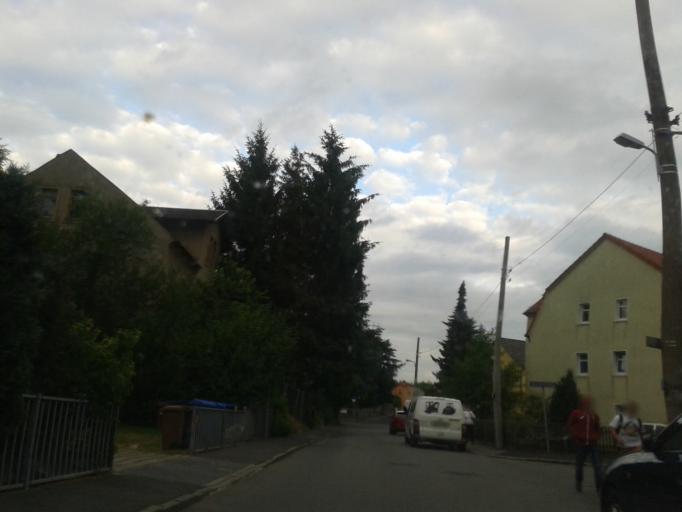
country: DE
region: Saxony
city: Albertstadt
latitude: 51.1099
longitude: 13.7700
